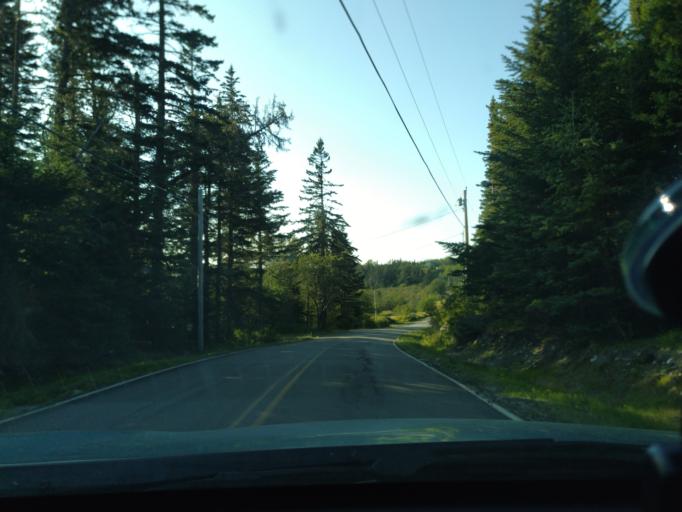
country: US
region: Maine
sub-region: Washington County
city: Machiasport
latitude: 44.6635
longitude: -67.2373
